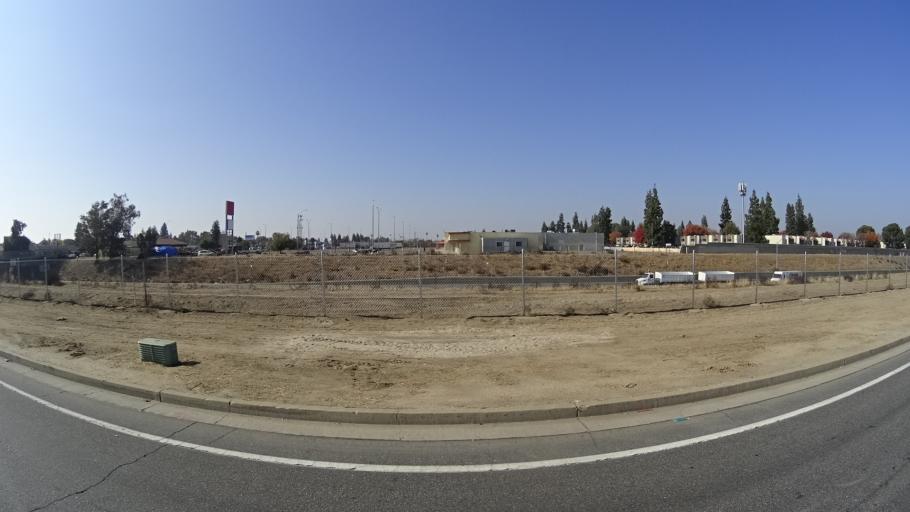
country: US
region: California
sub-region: Kern County
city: Bakersfield
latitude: 35.3332
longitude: -119.0388
